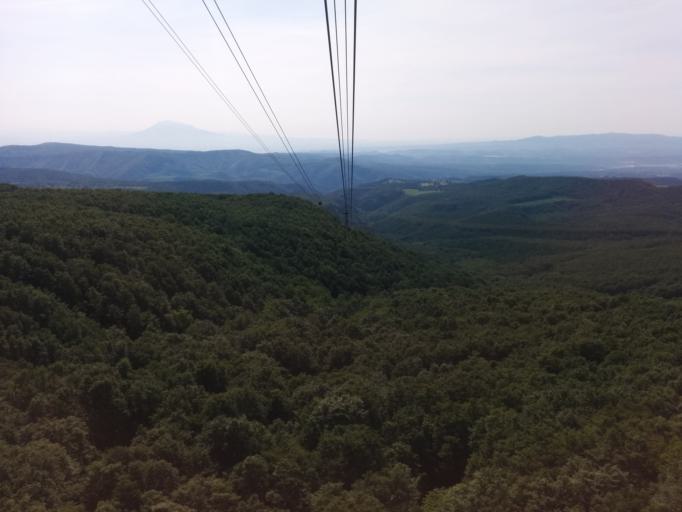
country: JP
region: Aomori
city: Aomori Shi
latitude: 40.6787
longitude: 140.8442
